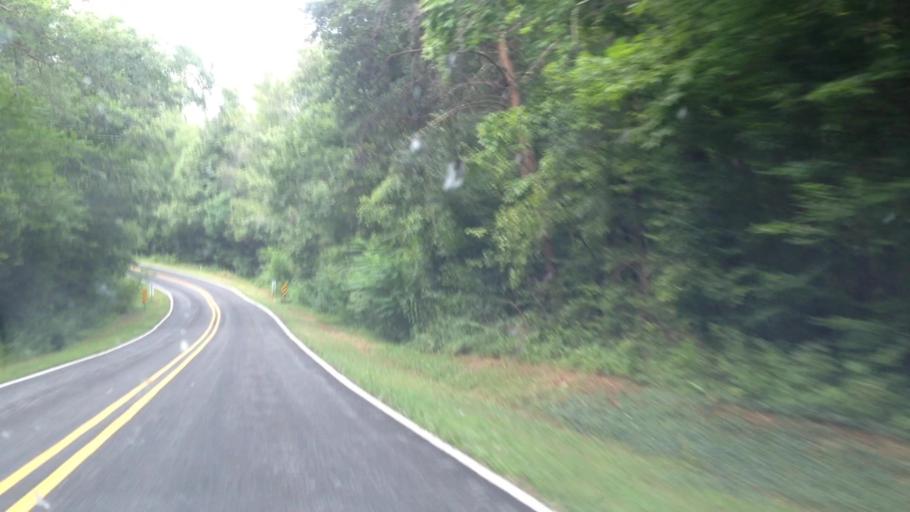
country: US
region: North Carolina
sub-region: Rockingham County
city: Mayodan
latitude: 36.4293
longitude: -80.0862
